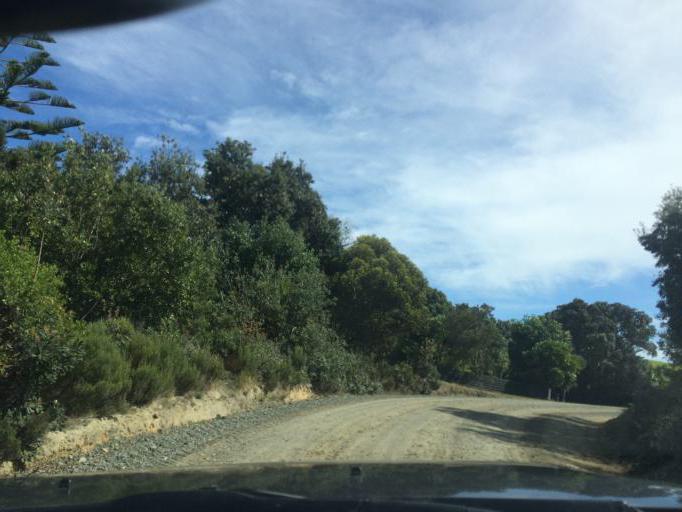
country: NZ
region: Northland
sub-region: Kaipara District
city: Dargaville
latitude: -35.9539
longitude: 173.7639
